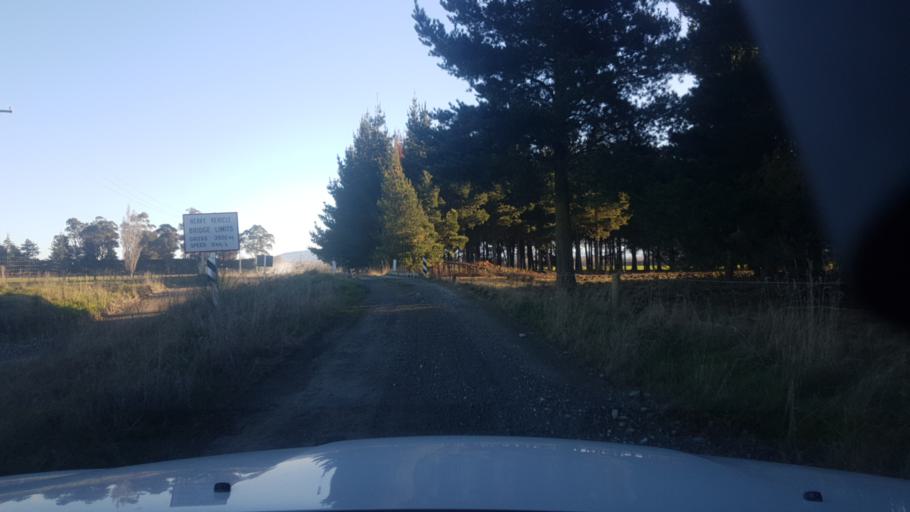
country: NZ
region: Canterbury
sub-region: Timaru District
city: Pleasant Point
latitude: -44.0756
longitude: 171.3072
